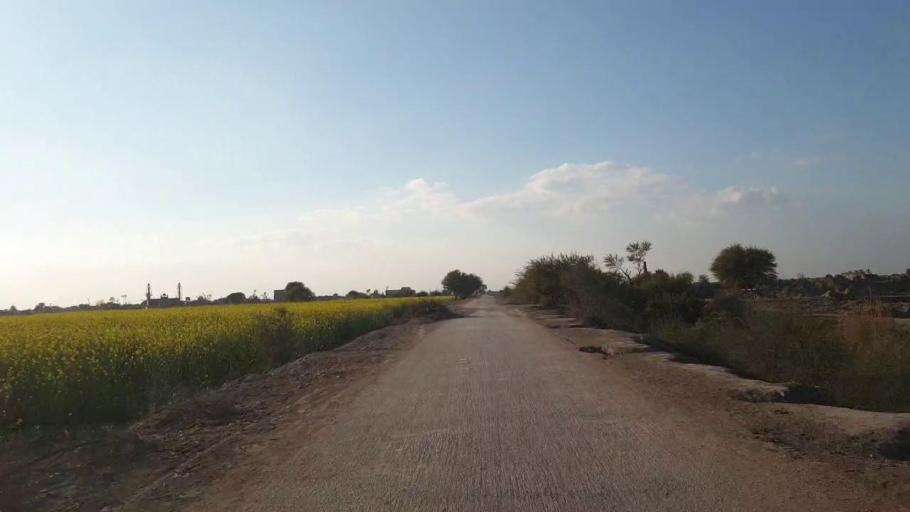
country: PK
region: Sindh
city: Shahpur Chakar
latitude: 26.1449
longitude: 68.5385
